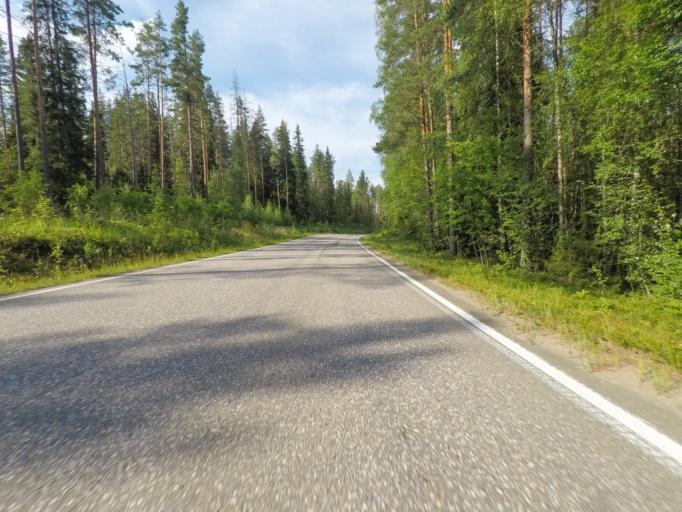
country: FI
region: Southern Savonia
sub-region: Savonlinna
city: Sulkava
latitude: 61.7674
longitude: 28.2355
